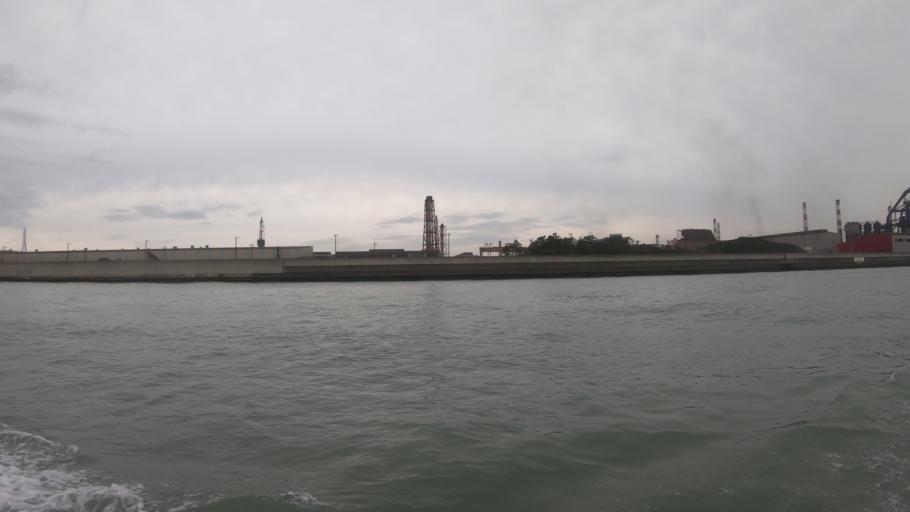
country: JP
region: Kanagawa
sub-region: Kawasaki-shi
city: Kawasaki
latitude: 35.4674
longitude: 139.7238
